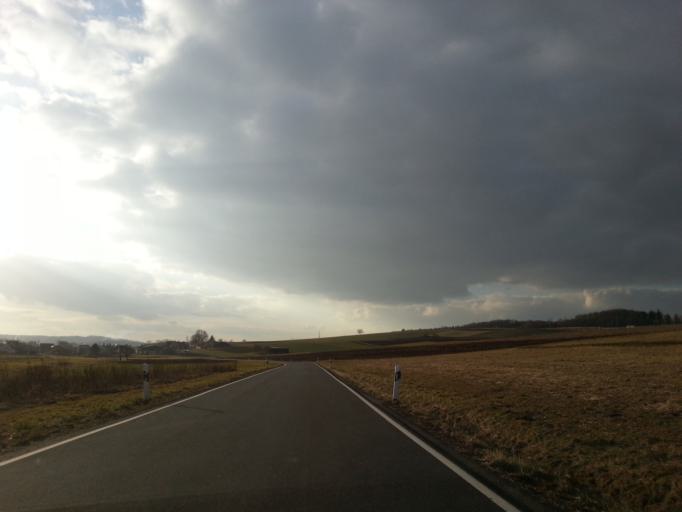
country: DE
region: Bavaria
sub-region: Regierungsbezirk Unterfranken
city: Holzkirchen
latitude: 49.7628
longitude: 9.6789
